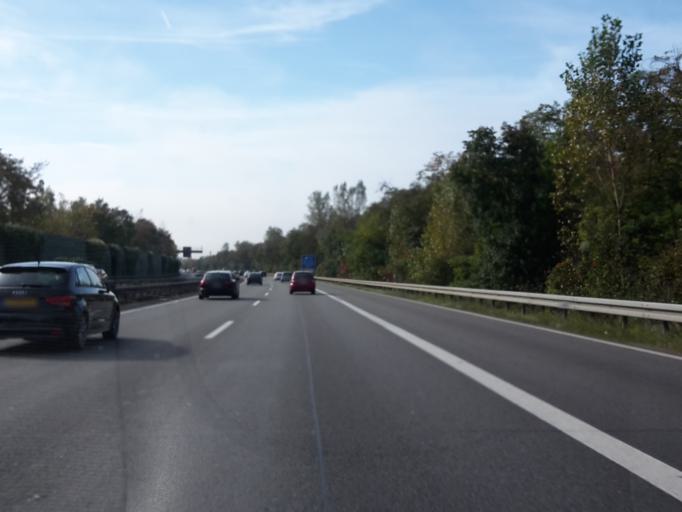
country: DE
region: Hesse
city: Pfungstadt
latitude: 49.8228
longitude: 8.6306
